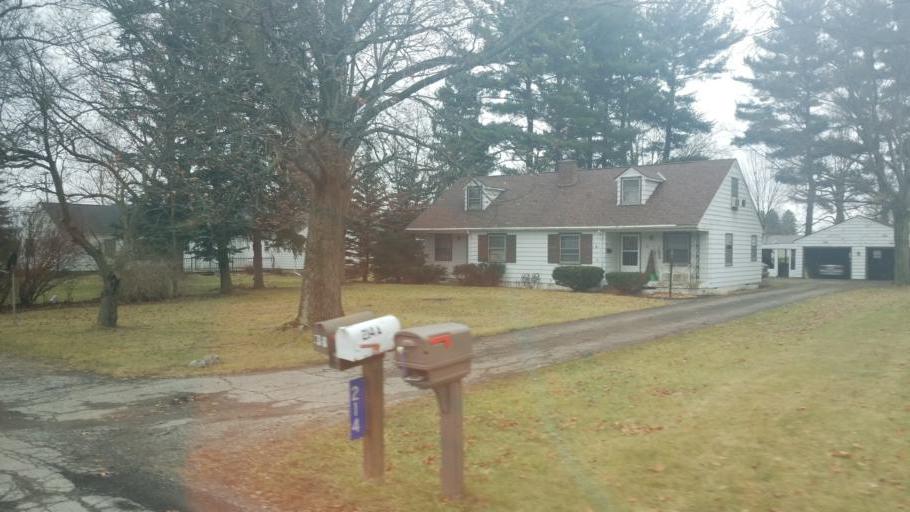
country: US
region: Ohio
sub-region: Crawford County
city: Galion
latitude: 40.7494
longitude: -82.7867
